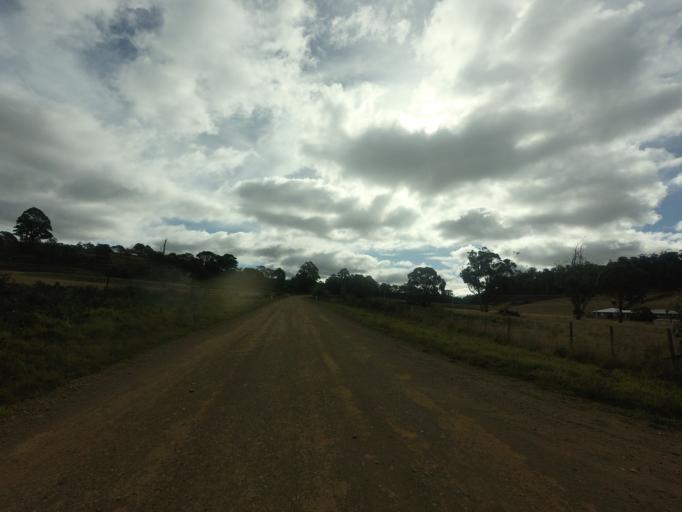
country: AU
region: Tasmania
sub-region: Brighton
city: Bridgewater
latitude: -42.4195
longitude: 147.4194
